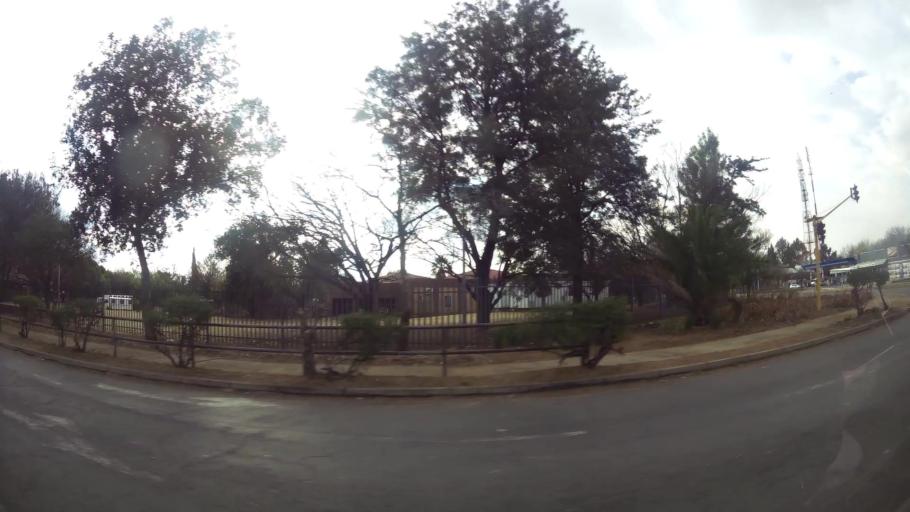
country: ZA
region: Orange Free State
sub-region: Fezile Dabi District Municipality
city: Sasolburg
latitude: -26.8181
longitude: 27.8302
